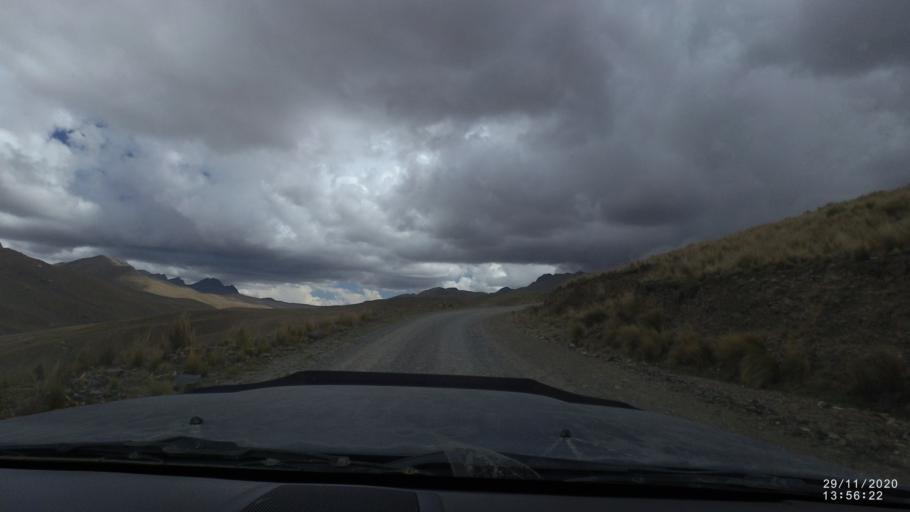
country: BO
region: Cochabamba
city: Sipe Sipe
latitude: -17.1757
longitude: -66.3591
